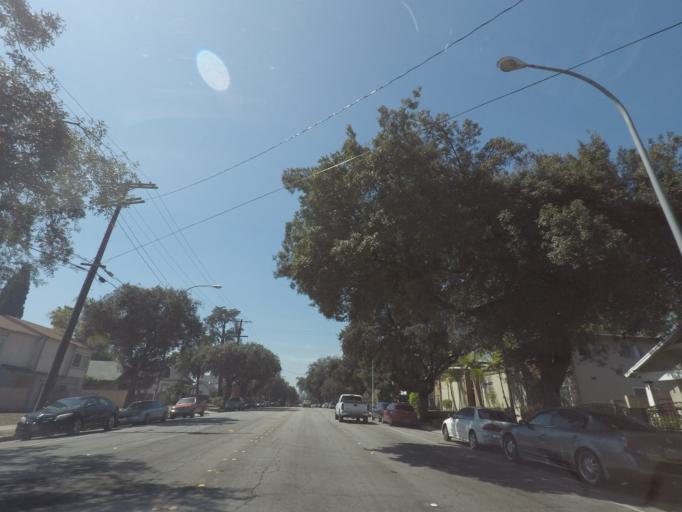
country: US
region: California
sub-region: Los Angeles County
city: Pasadena
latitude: 34.1578
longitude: -118.1343
